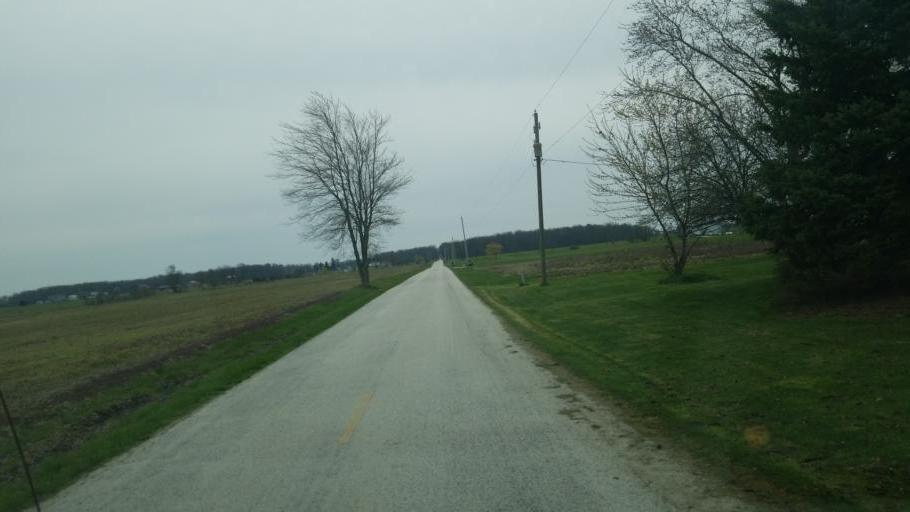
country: US
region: Ohio
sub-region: Seneca County
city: Fostoria
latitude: 41.0574
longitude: -83.4208
